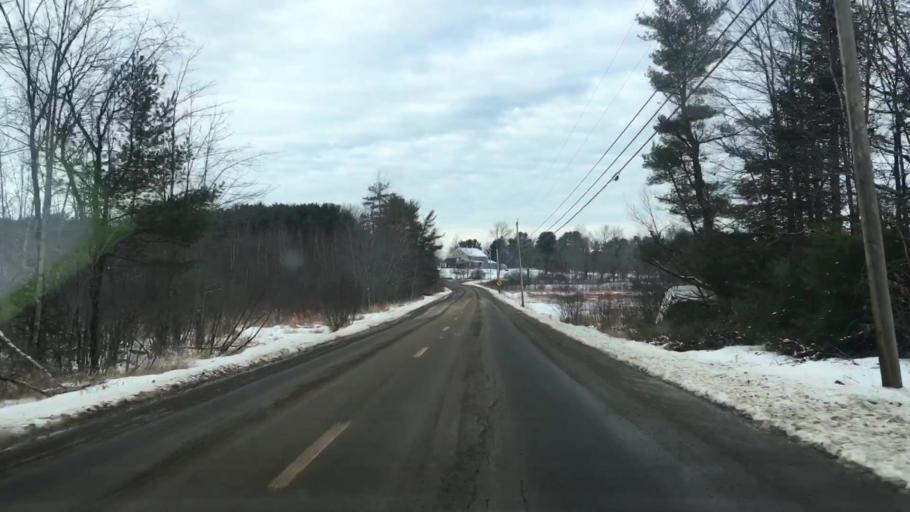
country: US
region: Maine
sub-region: Lincoln County
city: Whitefield
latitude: 44.2334
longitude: -69.6165
